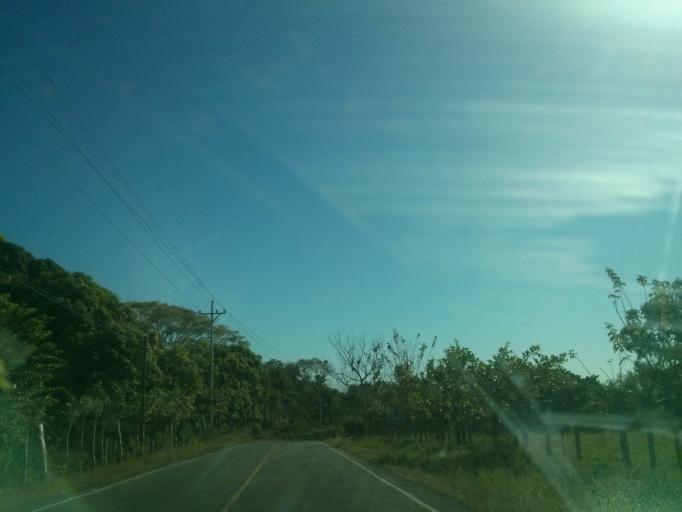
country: CR
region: Puntarenas
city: Paquera
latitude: 9.7028
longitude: -85.0394
